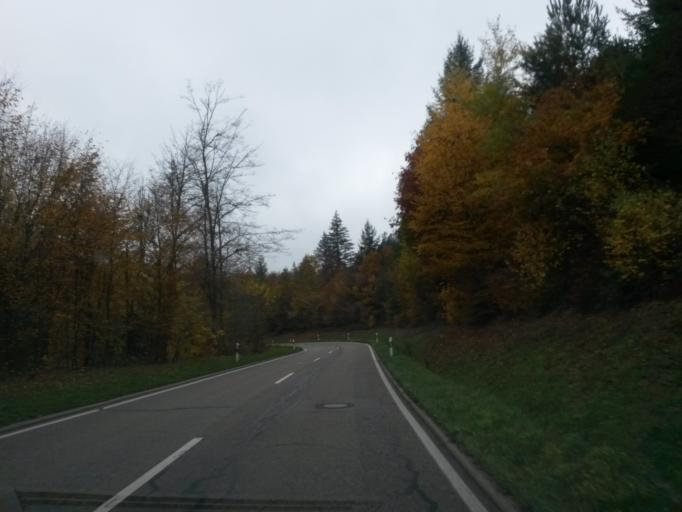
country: DE
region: Baden-Wuerttemberg
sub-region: Karlsruhe Region
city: Ettlingen
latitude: 48.8824
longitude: 8.4632
